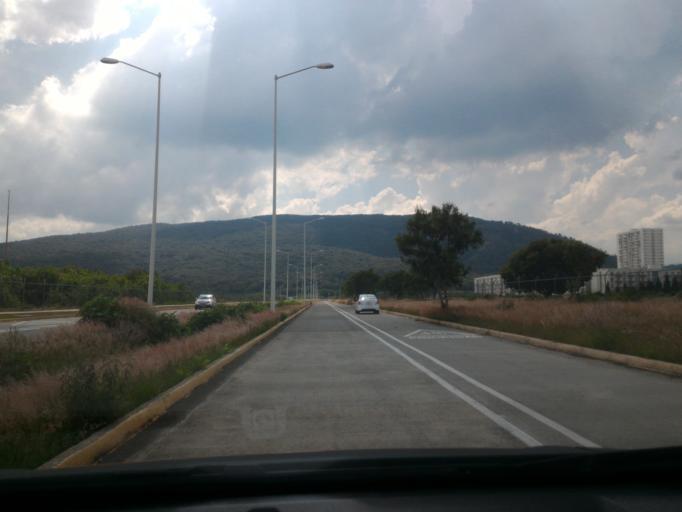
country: MX
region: Jalisco
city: Nuevo Mexico
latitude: 20.6906
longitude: -103.4677
